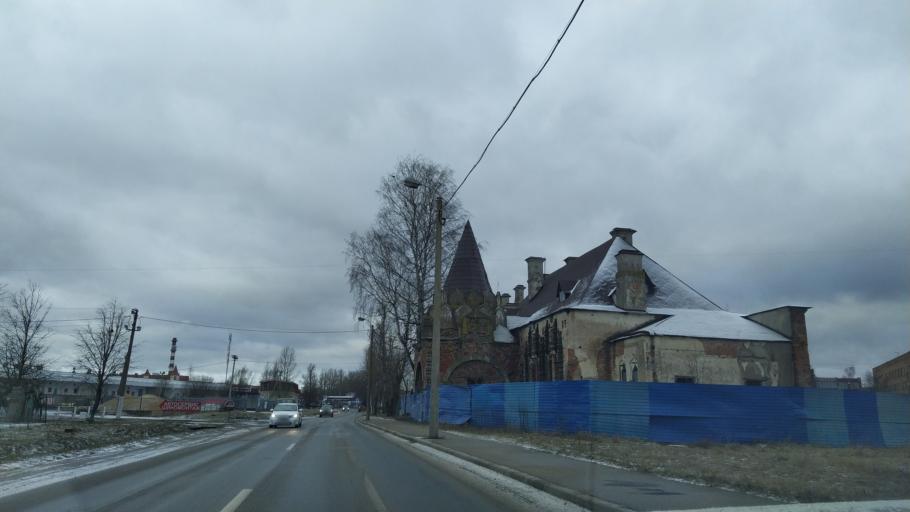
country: RU
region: St.-Petersburg
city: Pushkin
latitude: 59.7308
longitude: 30.3845
